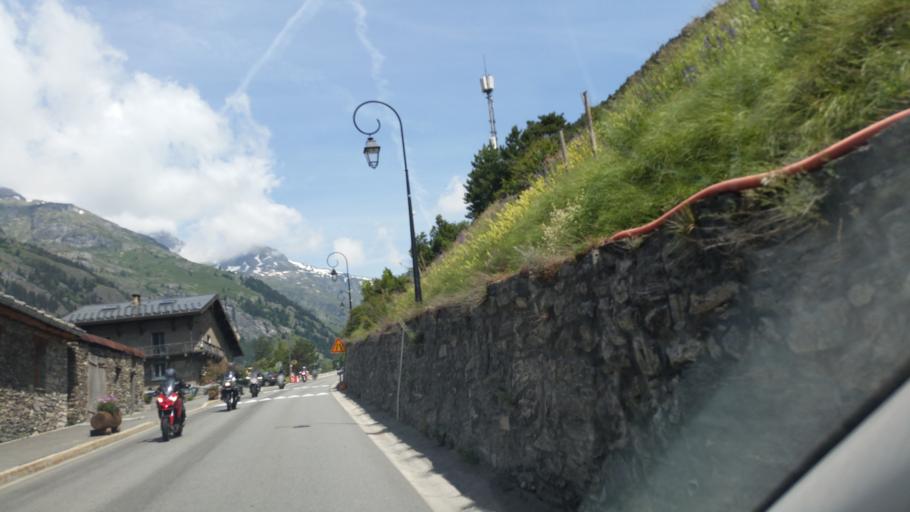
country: FR
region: Rhone-Alpes
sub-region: Departement de la Savoie
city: Modane
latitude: 45.2776
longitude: 6.8172
